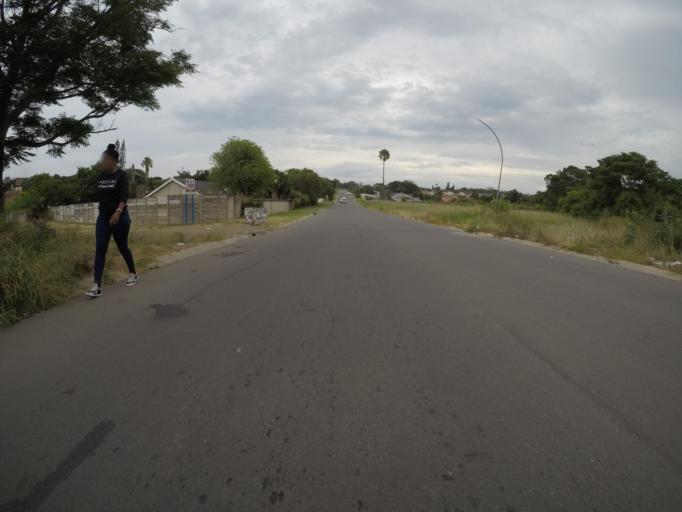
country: ZA
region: Eastern Cape
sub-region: Buffalo City Metropolitan Municipality
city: East London
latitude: -33.0015
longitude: 27.8580
